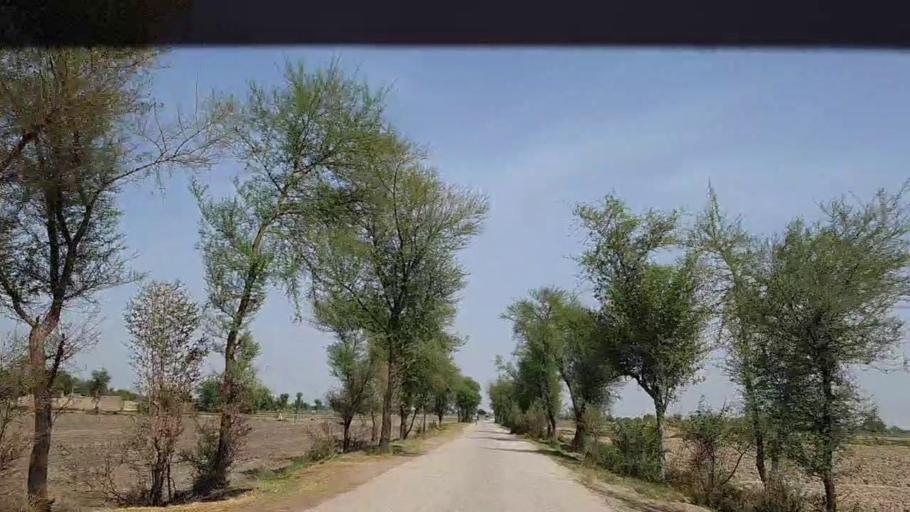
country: PK
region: Sindh
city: Phulji
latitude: 26.9544
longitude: 67.7129
